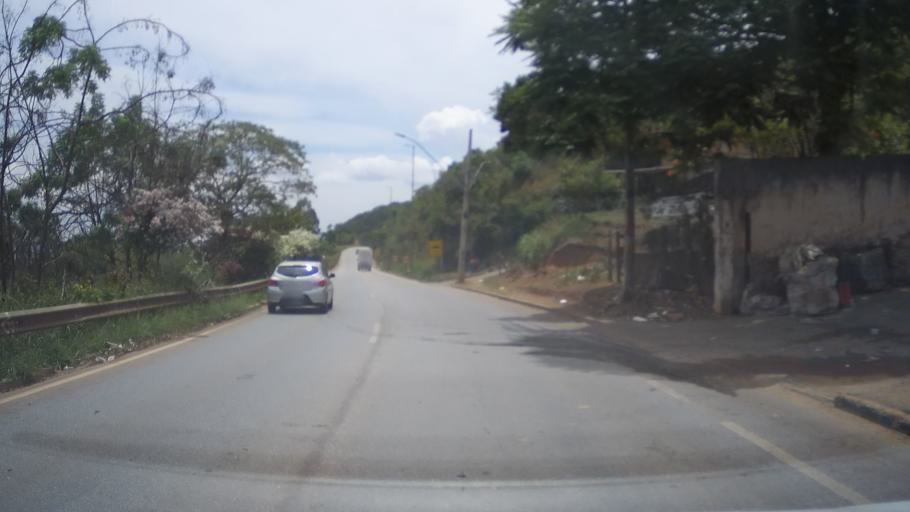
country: BR
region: Minas Gerais
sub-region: Nova Lima
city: Nova Lima
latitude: -19.9999
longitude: -43.8872
